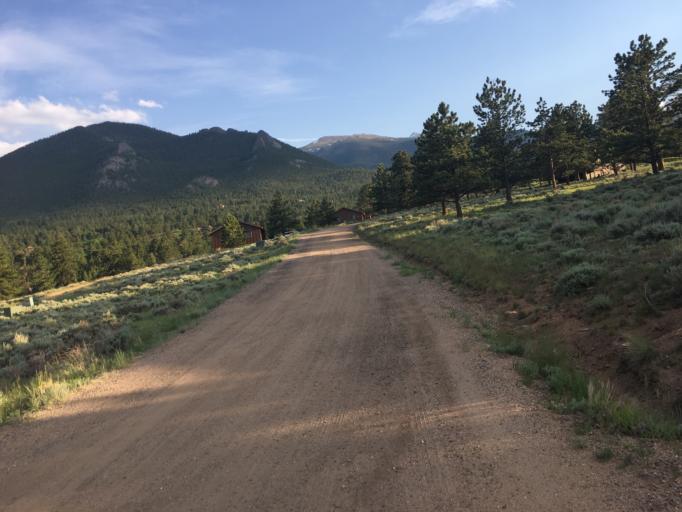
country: US
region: Colorado
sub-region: Larimer County
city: Estes Park
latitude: 40.3371
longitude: -105.5674
